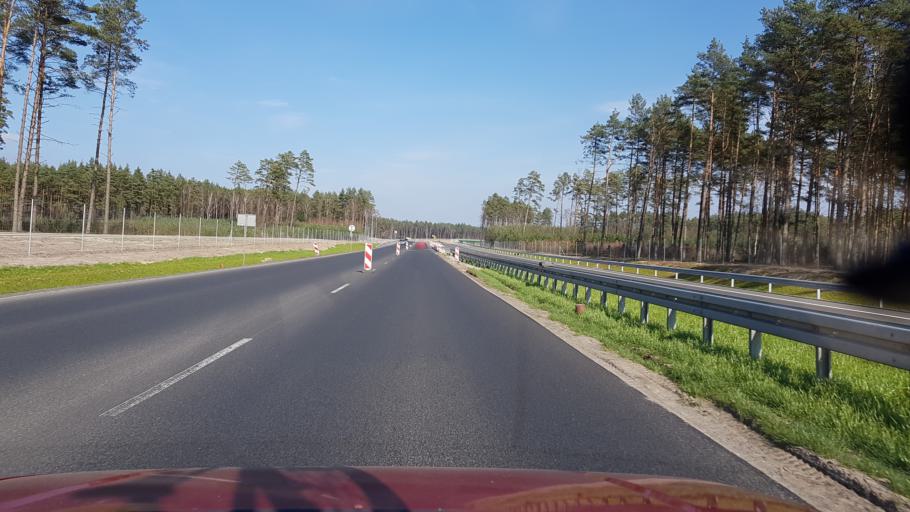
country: PL
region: West Pomeranian Voivodeship
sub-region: Powiat goleniowski
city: Goleniow
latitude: 53.6072
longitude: 14.8971
